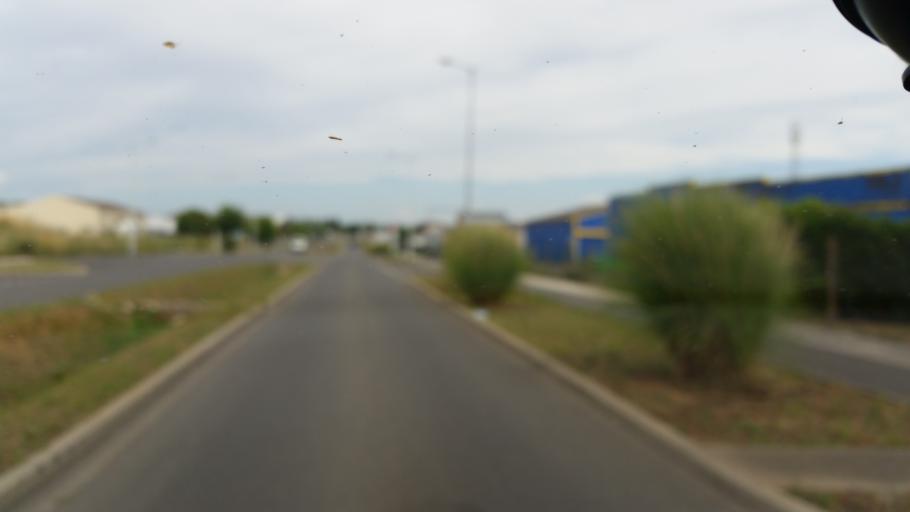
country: FR
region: Poitou-Charentes
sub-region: Departement de la Charente-Maritime
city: Surgeres
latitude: 46.1101
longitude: -0.7763
